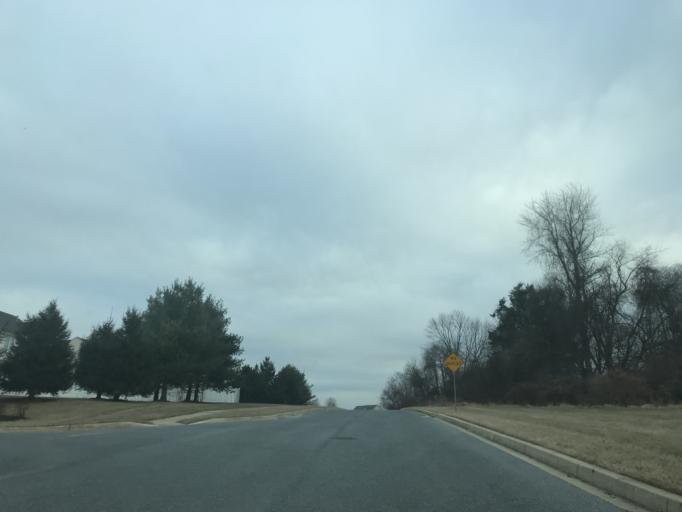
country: US
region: Maryland
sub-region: Carroll County
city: Eldersburg
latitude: 39.3749
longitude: -76.9277
